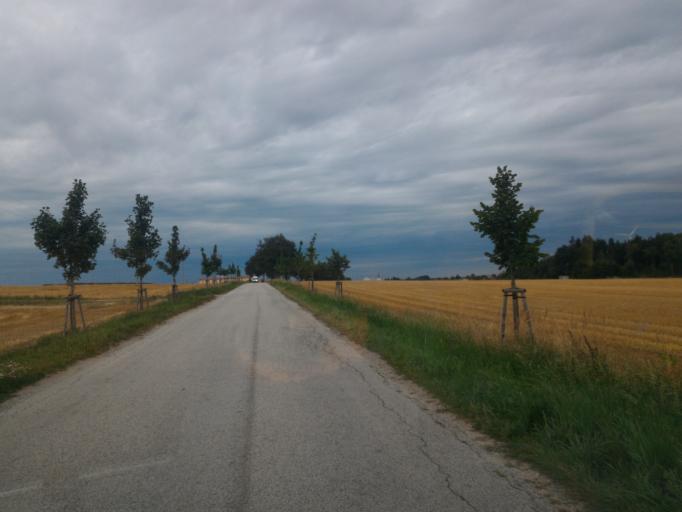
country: CZ
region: Vysocina
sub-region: Okres Jihlava
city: Trest'
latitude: 49.2408
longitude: 15.5697
